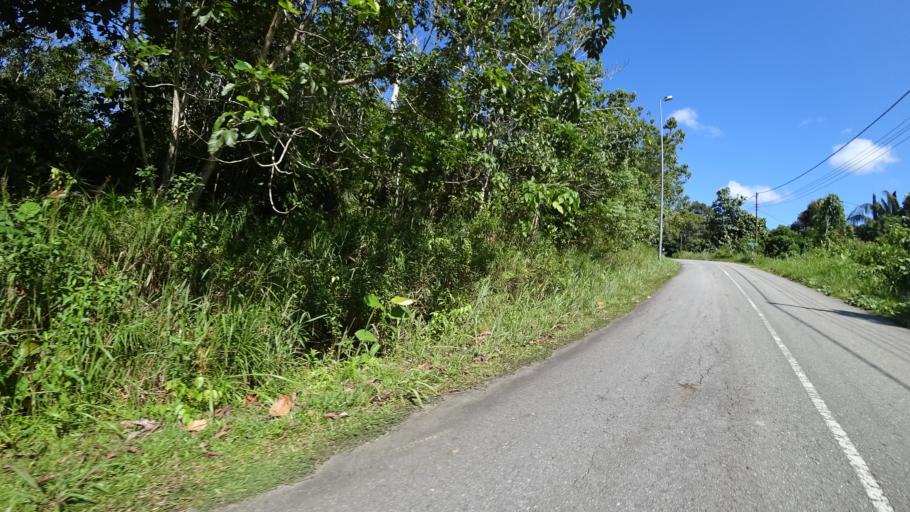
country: BN
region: Tutong
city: Tutong
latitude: 4.7451
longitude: 114.7858
